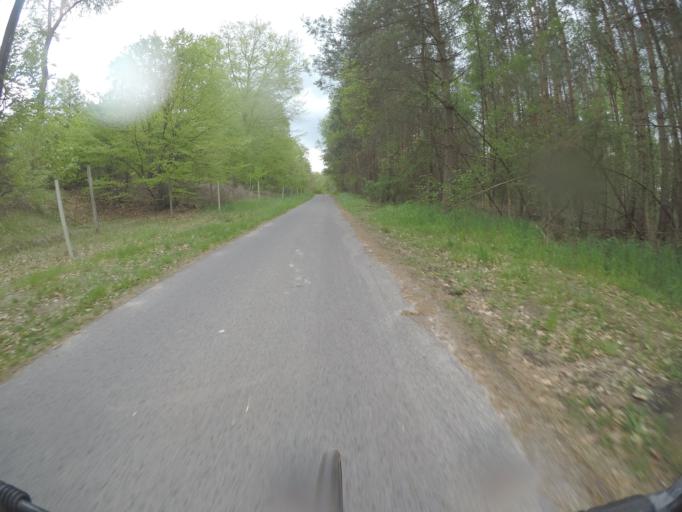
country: DE
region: Brandenburg
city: Biesenthal
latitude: 52.7935
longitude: 13.6296
